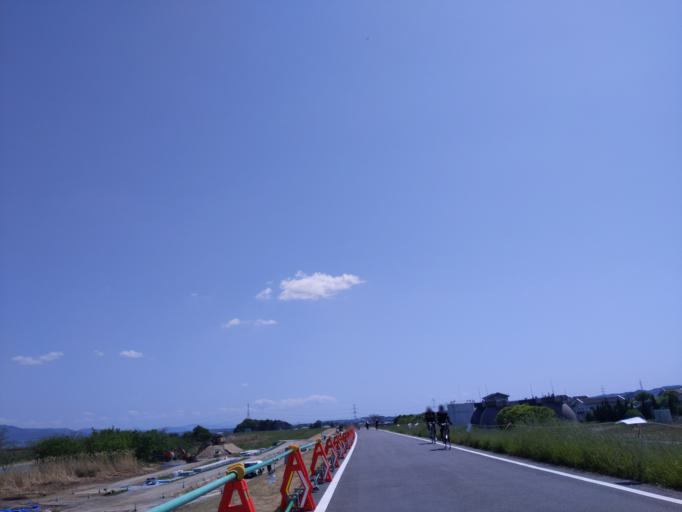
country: JP
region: Kyoto
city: Tanabe
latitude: 34.7761
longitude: 135.8002
